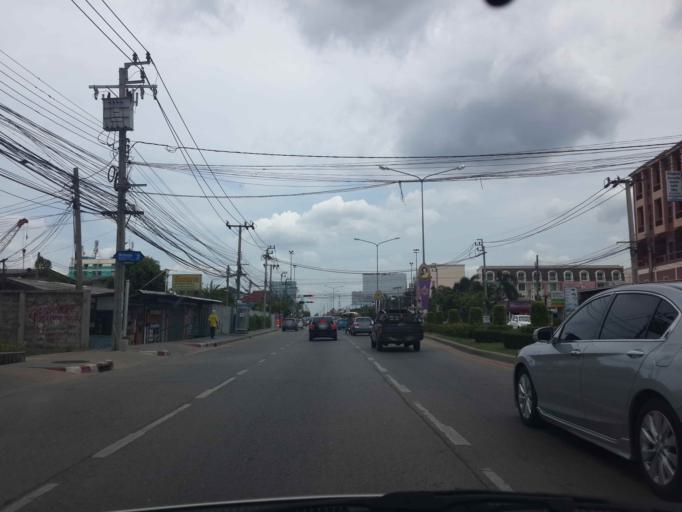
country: TH
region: Bangkok
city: Khan Na Yao
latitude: 13.8591
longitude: 100.6945
